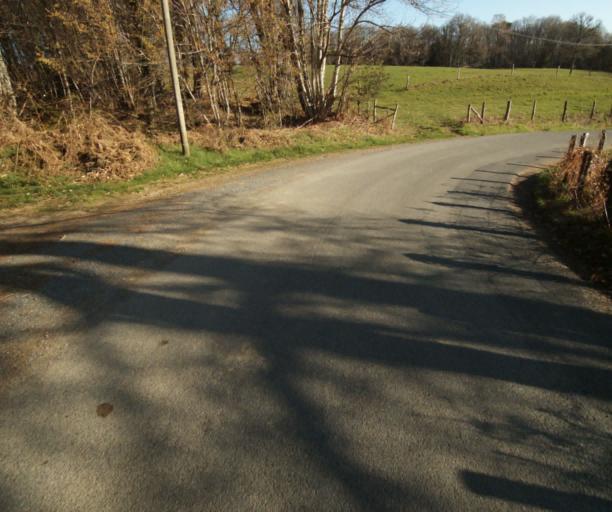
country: FR
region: Limousin
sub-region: Departement de la Correze
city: Seilhac
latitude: 45.3596
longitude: 1.7337
